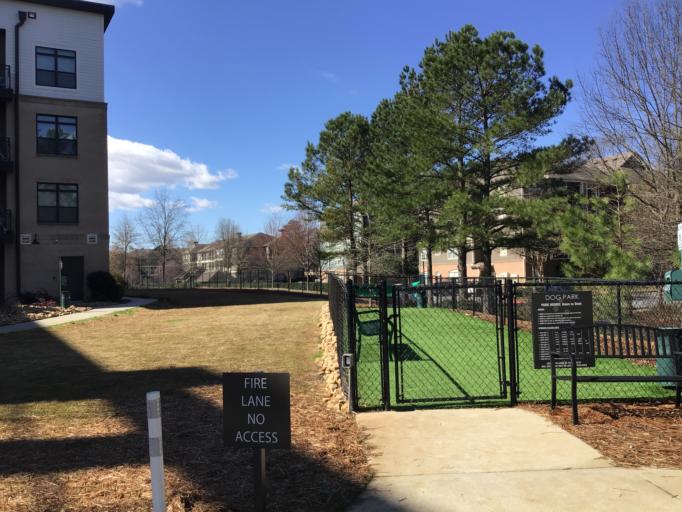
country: US
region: Georgia
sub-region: DeKalb County
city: Chamblee
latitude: 33.8892
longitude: -84.3155
